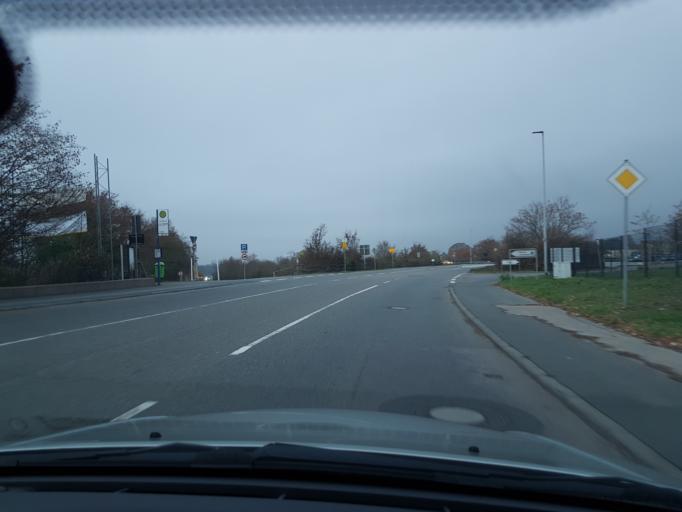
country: DE
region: Hesse
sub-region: Regierungsbezirk Darmstadt
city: Eltville
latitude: 50.0227
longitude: 8.1102
